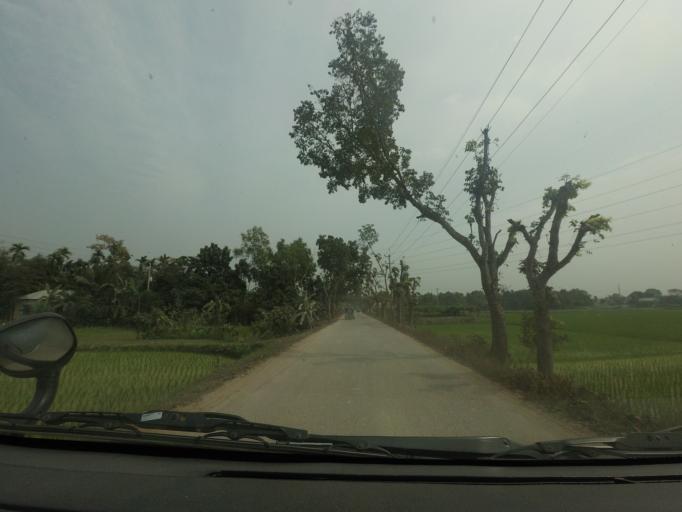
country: BD
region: Dhaka
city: Kishorganj
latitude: 24.3441
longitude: 90.7736
